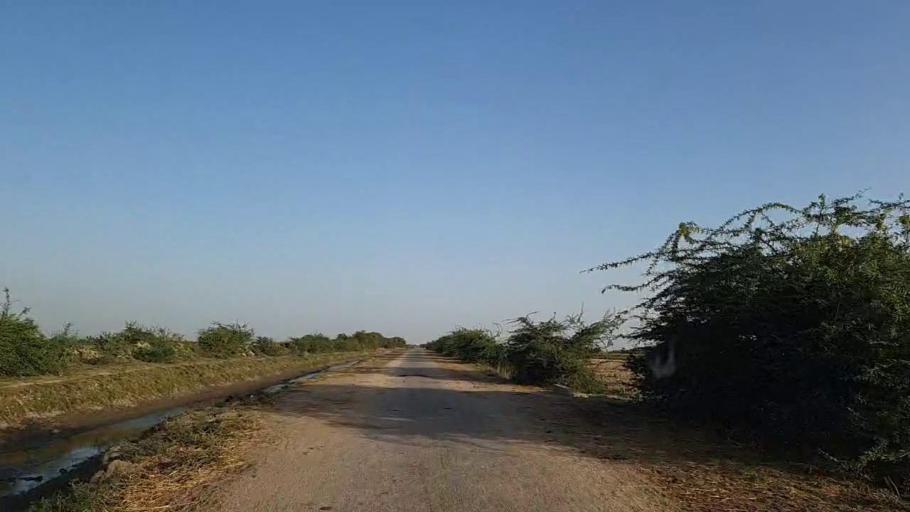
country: PK
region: Sindh
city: Jati
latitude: 24.4099
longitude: 68.3493
